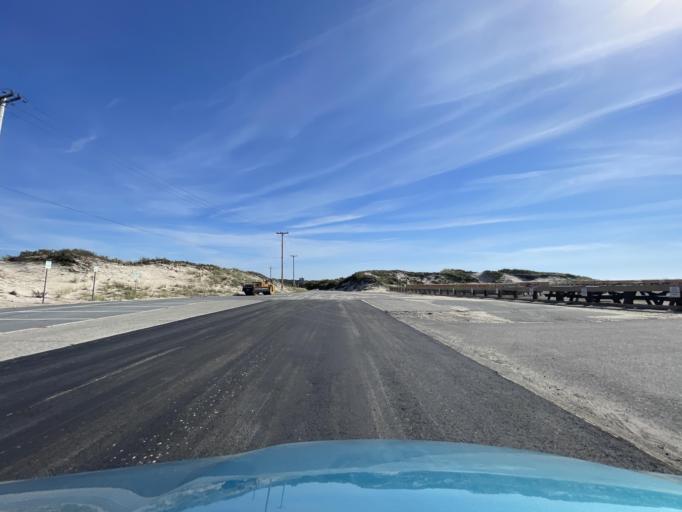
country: US
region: Massachusetts
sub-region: Bristol County
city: Head of Westport
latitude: 41.5065
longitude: -71.0538
